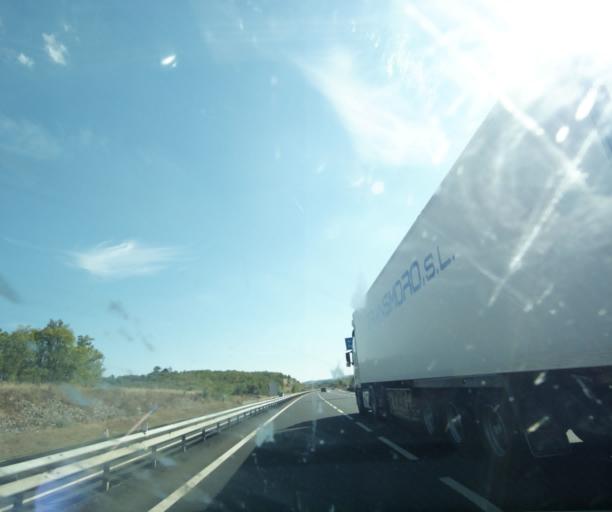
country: FR
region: Limousin
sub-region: Departement de la Correze
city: Brive-la-Gaillarde
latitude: 45.0378
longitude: 1.5242
